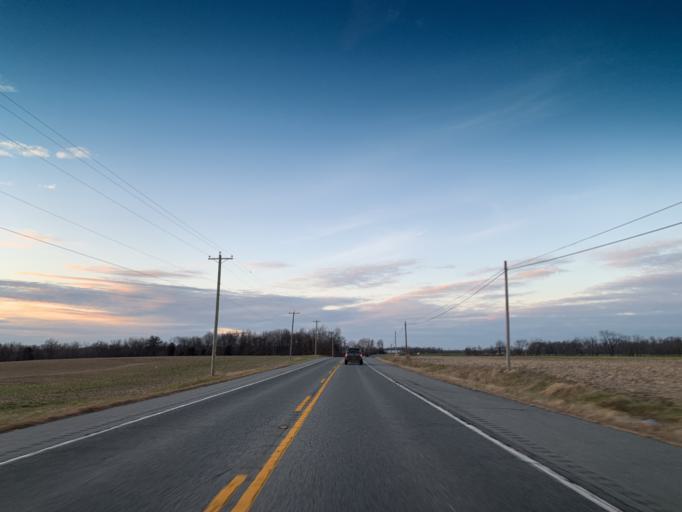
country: US
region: Delaware
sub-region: New Castle County
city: Middletown
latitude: 39.4414
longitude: -75.8646
